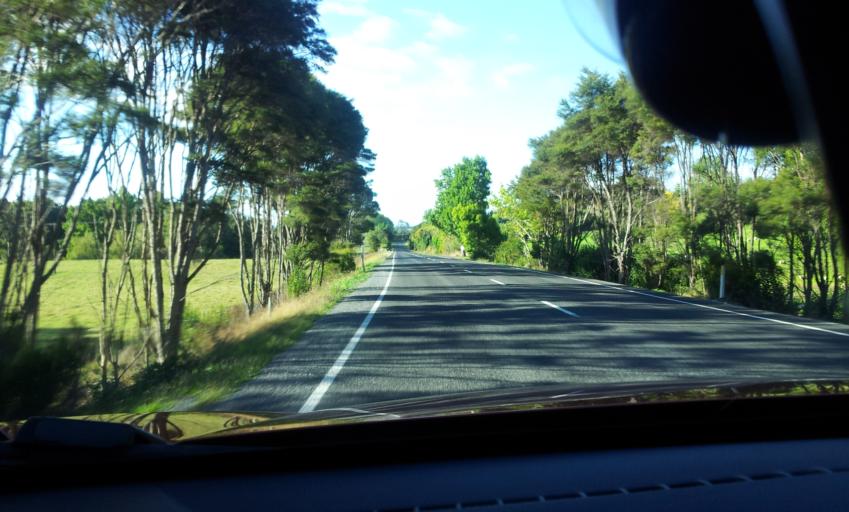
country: NZ
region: Waikato
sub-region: Hauraki District
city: Ngatea
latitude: -37.3275
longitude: 175.4046
